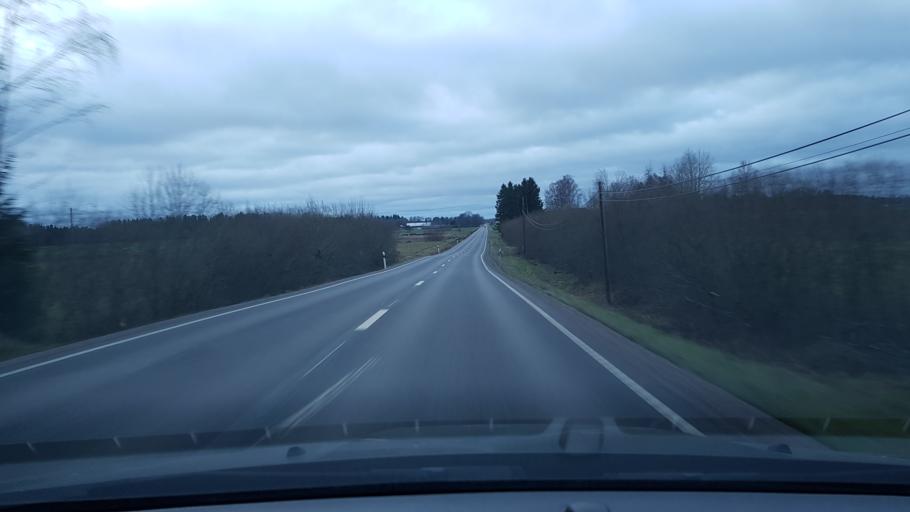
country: SE
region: Uppsala
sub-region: Uppsala Kommun
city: Vattholma
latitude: 59.9489
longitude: 17.9340
